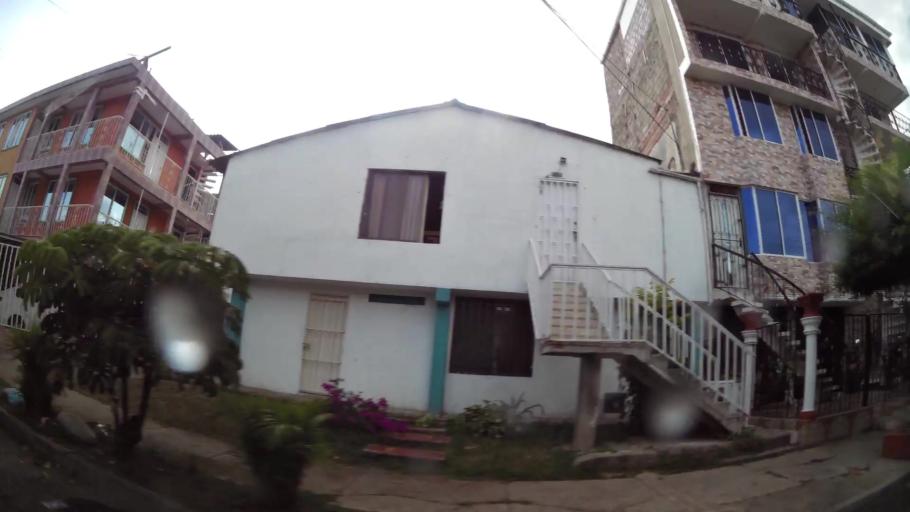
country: CO
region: Valle del Cauca
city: Cali
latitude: 3.4671
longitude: -76.4892
